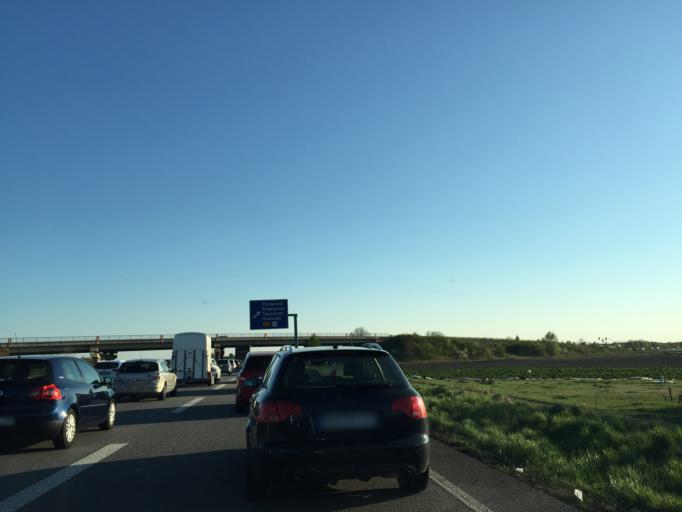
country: DE
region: Hesse
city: Pfungstadt
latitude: 49.8041
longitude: 8.5724
